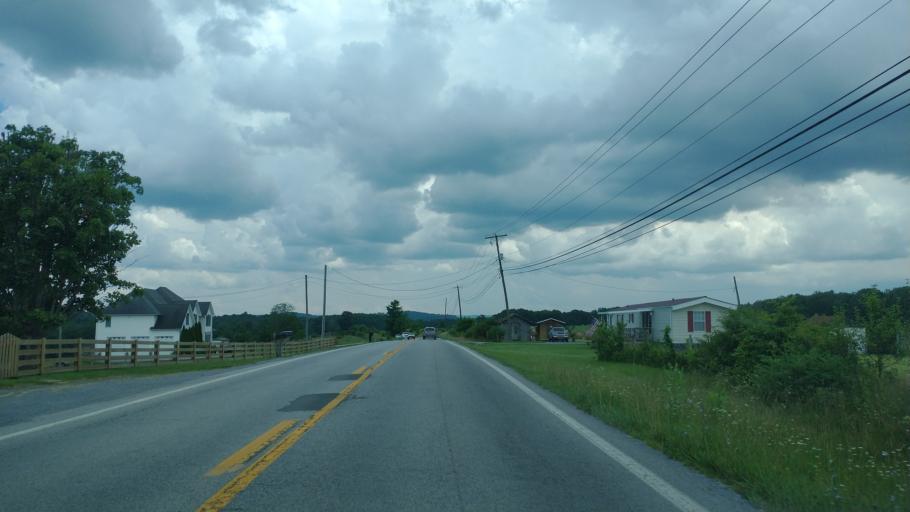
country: US
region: West Virginia
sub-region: Mercer County
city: Athens
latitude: 37.4520
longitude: -81.0077
